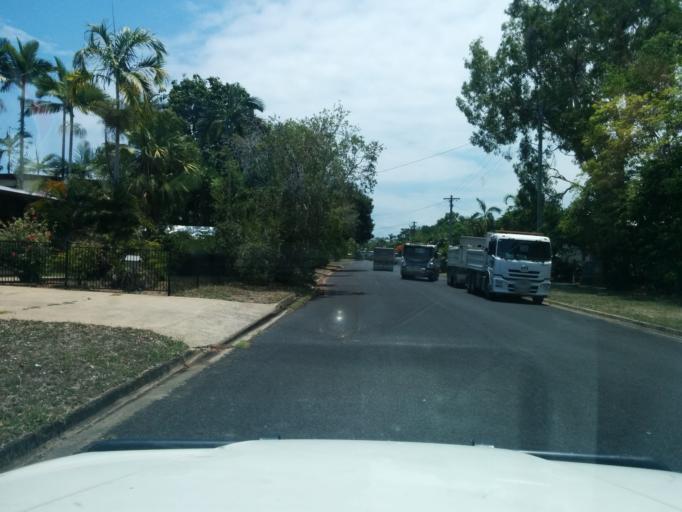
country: AU
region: Queensland
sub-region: Cairns
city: Yorkeys Knob
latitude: -16.8379
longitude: 145.7373
